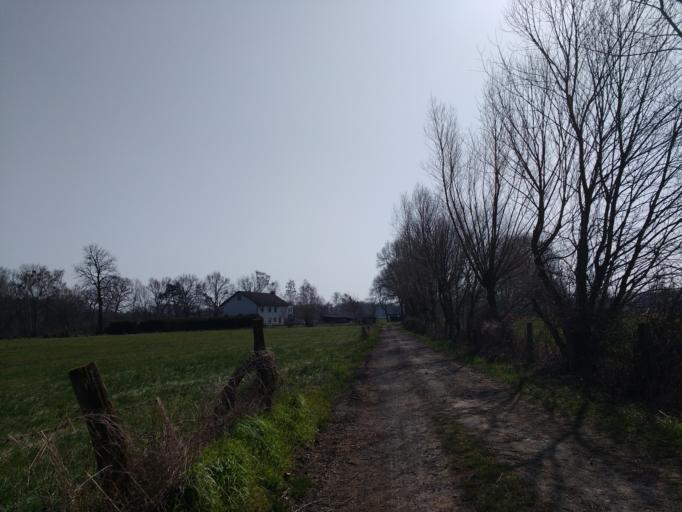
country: DE
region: North Rhine-Westphalia
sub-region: Regierungsbezirk Detmold
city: Salzkotten
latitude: 51.7230
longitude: 8.6529
